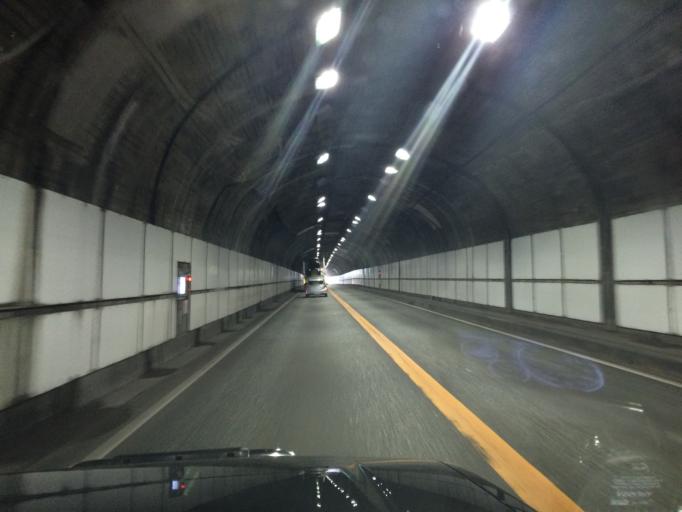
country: JP
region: Hyogo
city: Toyooka
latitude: 35.3525
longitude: 134.8345
